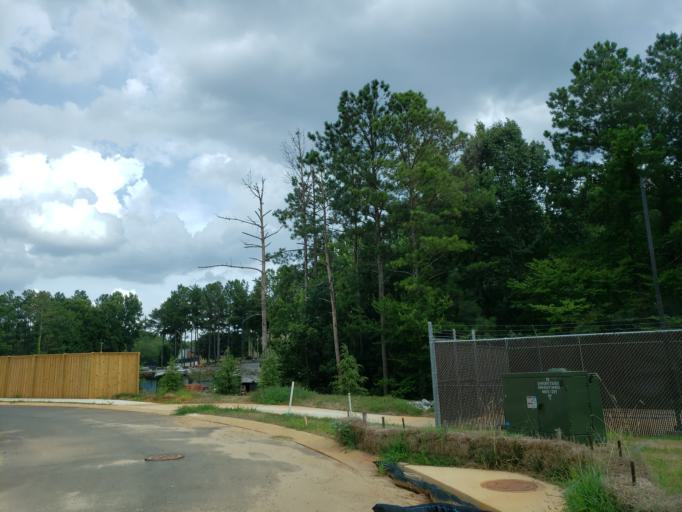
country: US
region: Georgia
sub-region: Fulton County
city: Milton
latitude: 34.1388
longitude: -84.2525
